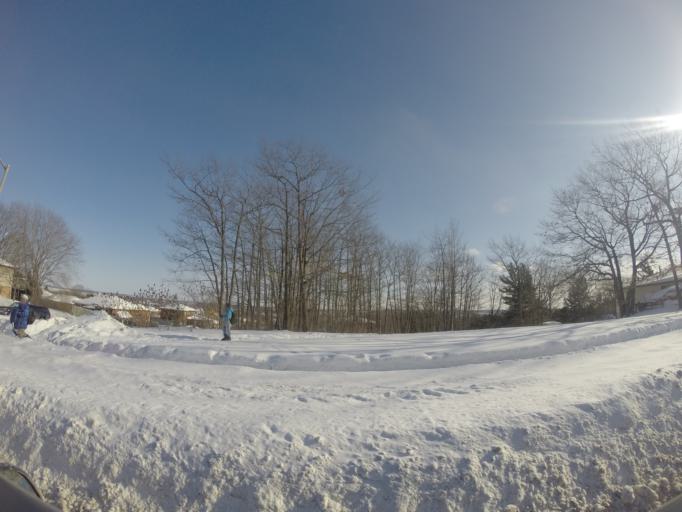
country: CA
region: Ontario
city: Barrie
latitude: 44.3875
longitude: -79.7193
